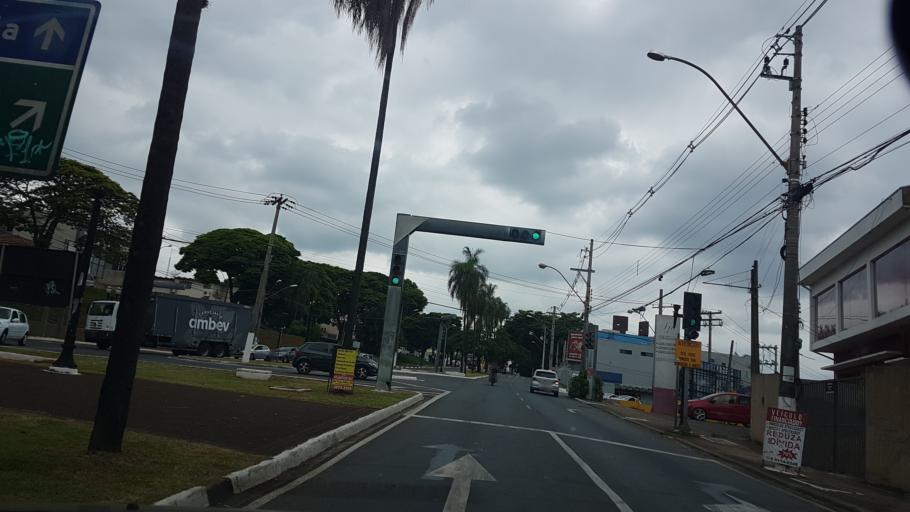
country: BR
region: Sao Paulo
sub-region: Paulinia
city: Paulinia
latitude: -22.7592
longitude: -47.1588
